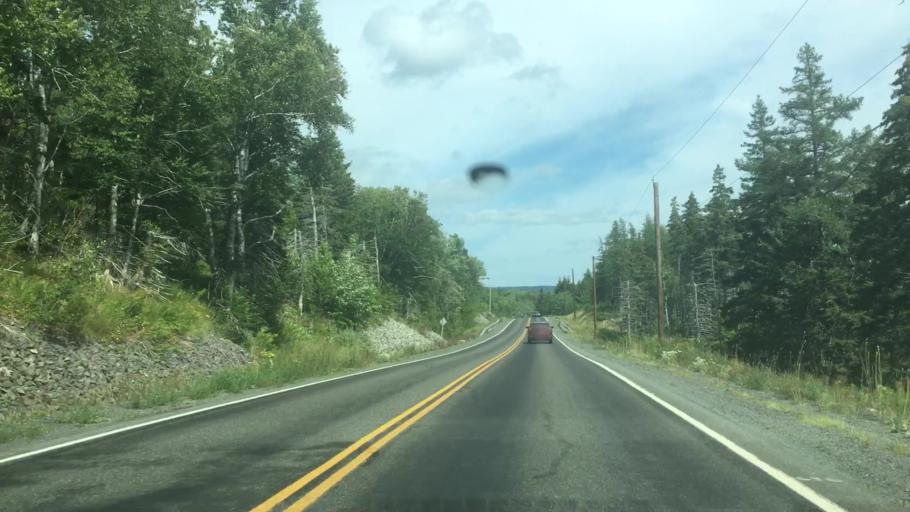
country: CA
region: Nova Scotia
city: Sydney Mines
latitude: 46.2152
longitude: -60.6200
